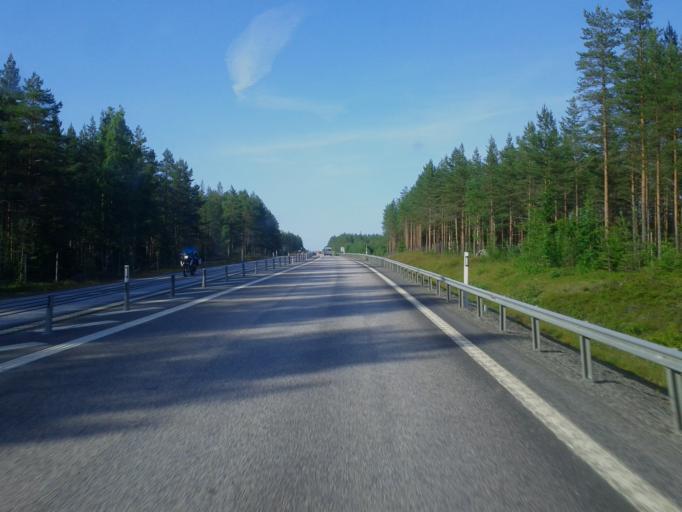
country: SE
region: Vaesterbotten
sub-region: Umea Kommun
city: Saevar
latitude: 63.9328
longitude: 20.6414
